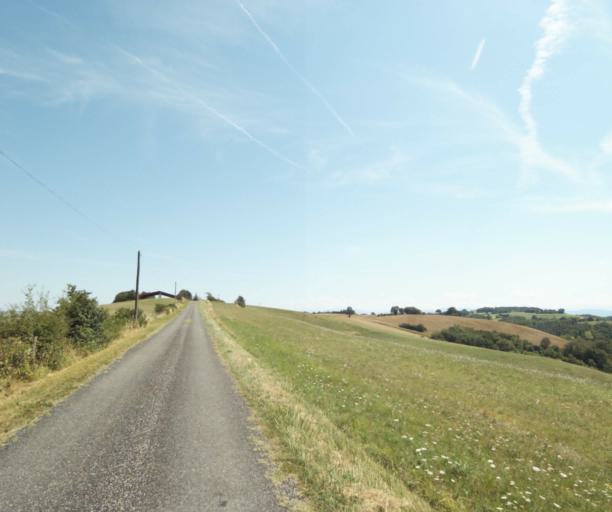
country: FR
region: Midi-Pyrenees
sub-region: Departement de l'Ariege
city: Lezat-sur-Leze
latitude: 43.2522
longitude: 1.3246
